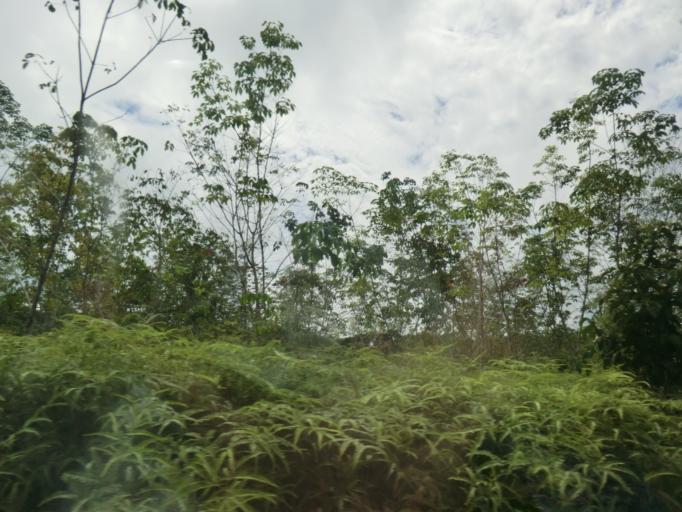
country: MY
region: Sarawak
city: Simanggang
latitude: 1.0603
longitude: 112.0361
